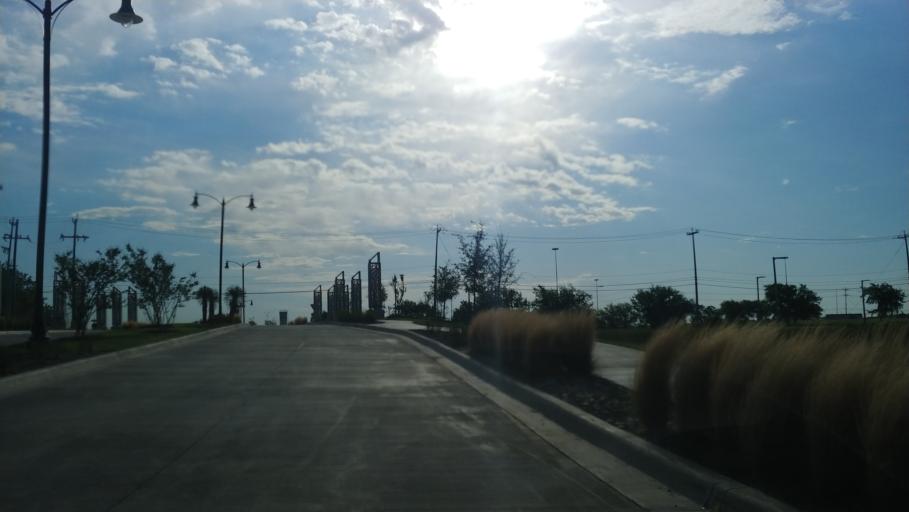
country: US
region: Texas
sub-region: Bexar County
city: Live Oak
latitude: 29.5678
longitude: -98.3384
